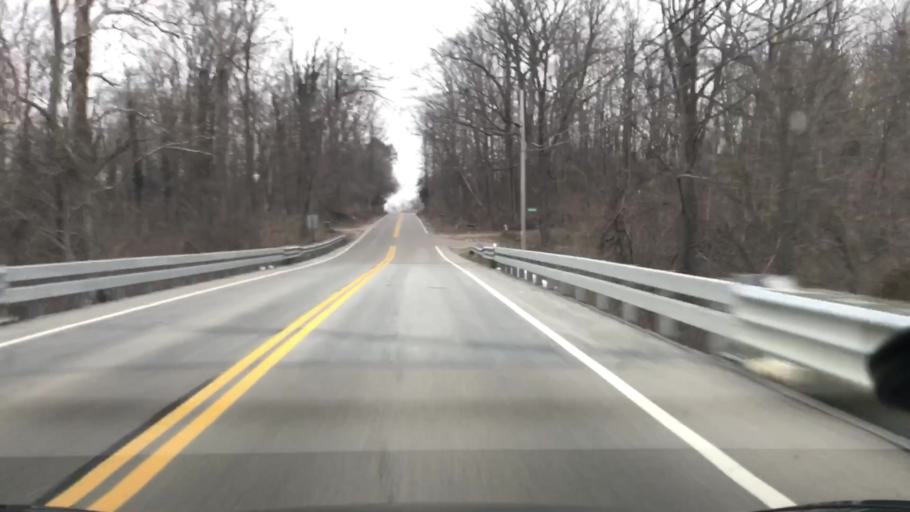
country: US
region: Ohio
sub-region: Clark County
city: Springfield
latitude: 39.8811
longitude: -83.8448
